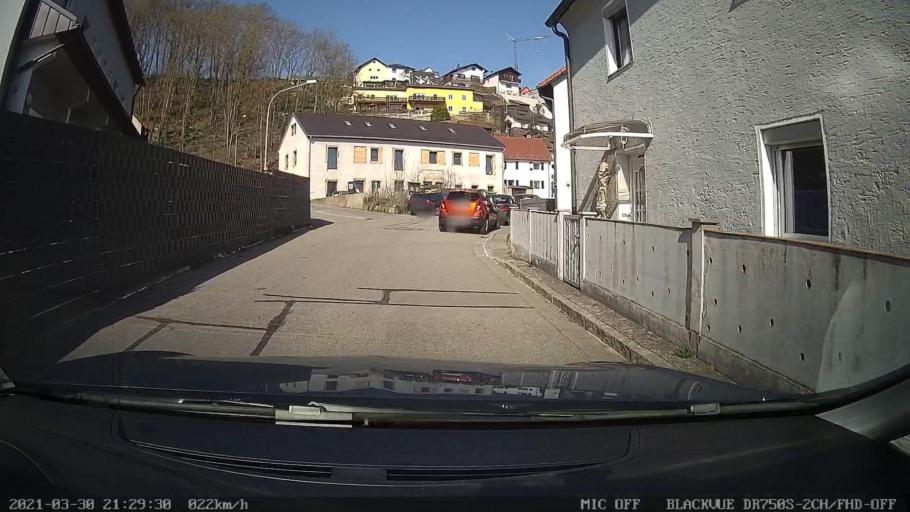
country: DE
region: Bavaria
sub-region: Upper Palatinate
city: Zeitlarn
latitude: 49.0938
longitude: 12.1068
